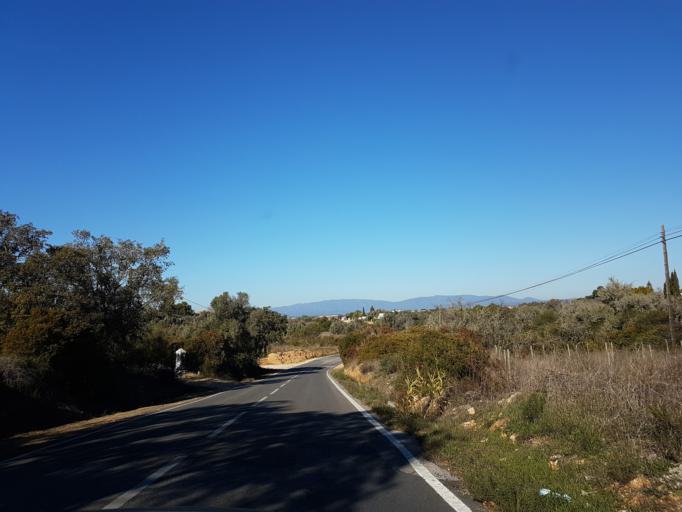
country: PT
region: Faro
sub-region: Lagoa
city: Carvoeiro
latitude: 37.1044
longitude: -8.4450
